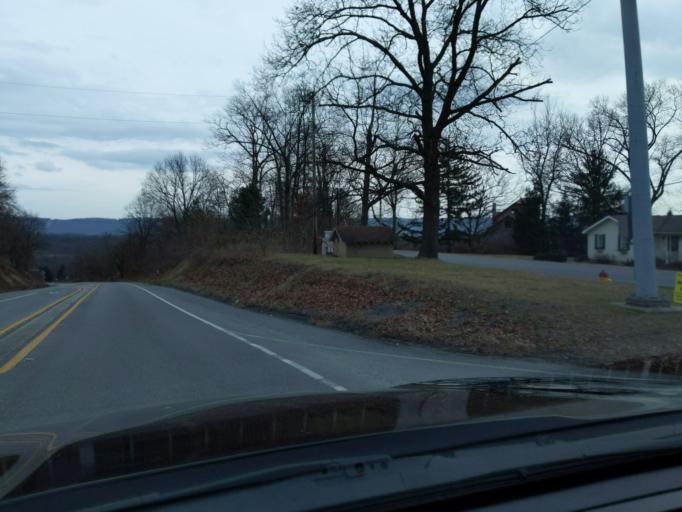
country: US
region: Pennsylvania
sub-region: Blair County
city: Lakemont
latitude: 40.4613
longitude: -78.3653
